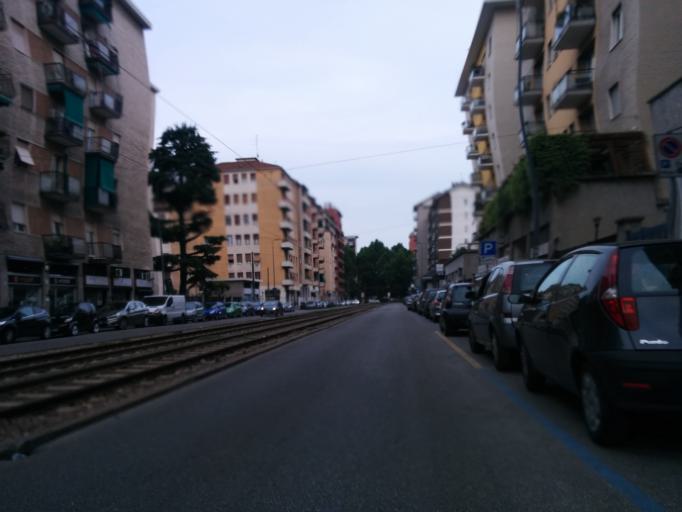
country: IT
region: Lombardy
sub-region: Citta metropolitana di Milano
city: Milano
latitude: 45.4512
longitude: 9.2179
